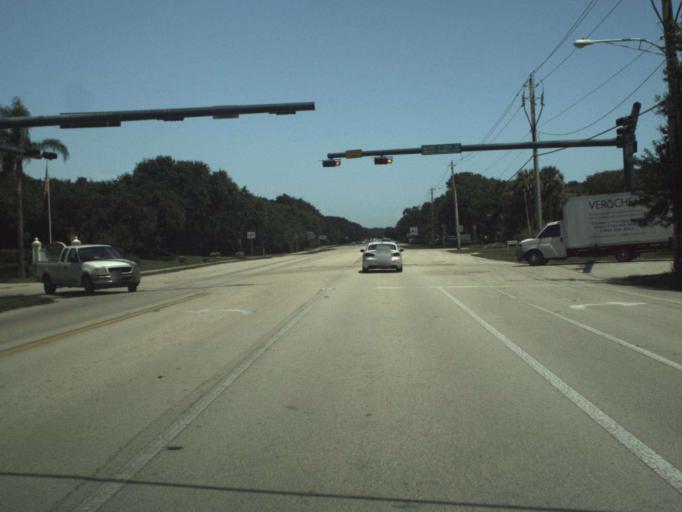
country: US
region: Florida
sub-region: Indian River County
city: Indian River Shores
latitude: 27.6918
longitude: -80.3708
